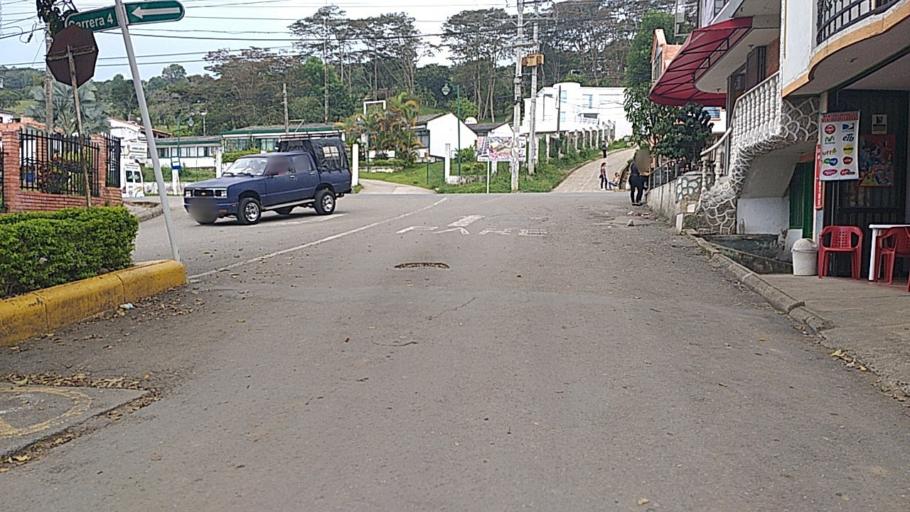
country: CO
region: Boyaca
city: Santana
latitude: 6.0559
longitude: -73.4815
